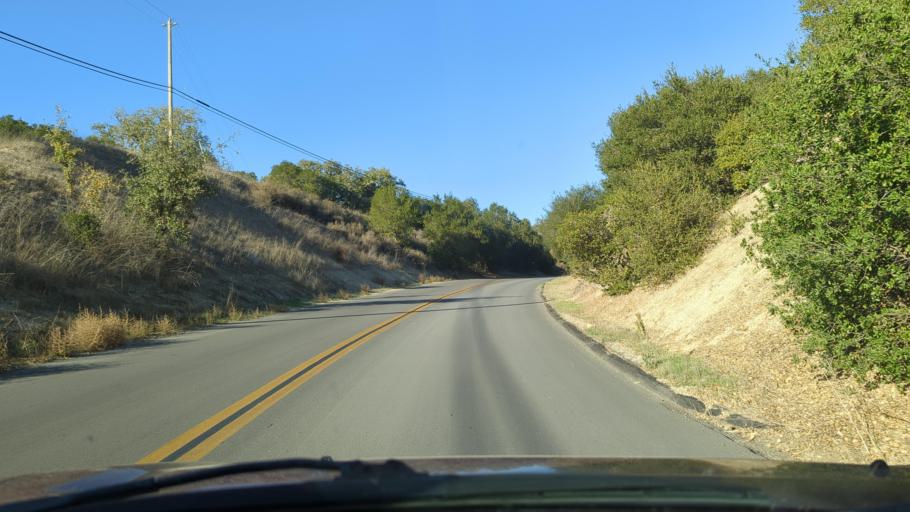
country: US
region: California
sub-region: Santa Barbara County
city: Santa Ynez
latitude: 34.5901
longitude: -120.0996
